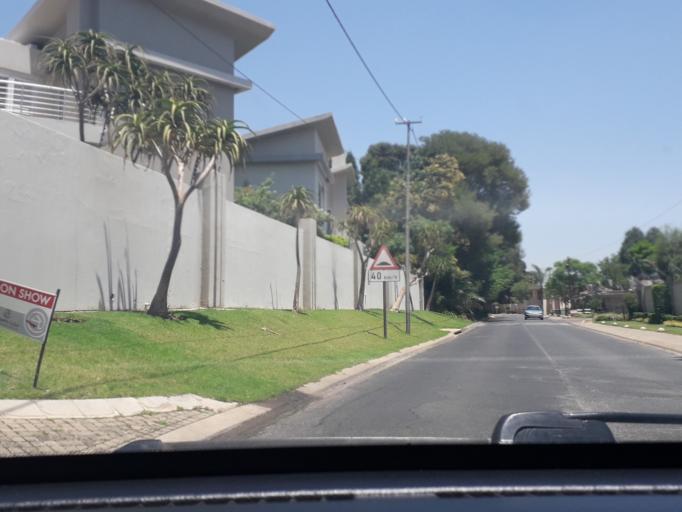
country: ZA
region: Gauteng
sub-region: City of Johannesburg Metropolitan Municipality
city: Johannesburg
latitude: -26.0889
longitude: 28.0514
